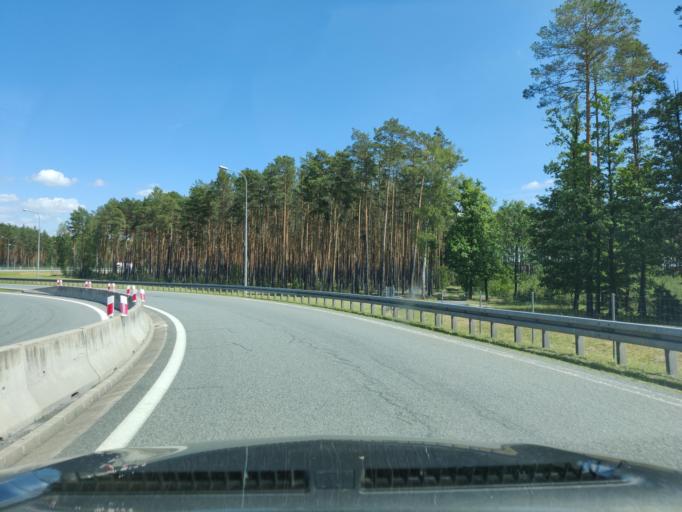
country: PL
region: Greater Poland Voivodeship
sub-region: Powiat nowotomyski
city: Nowy Tomysl
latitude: 52.3580
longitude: 16.1026
